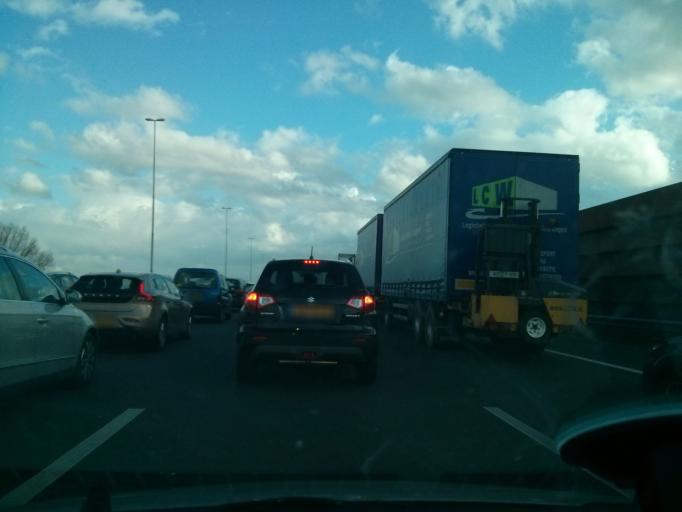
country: NL
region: Gelderland
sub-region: Gemeente Culemborg
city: Culemborg
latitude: 51.8896
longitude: 5.1992
